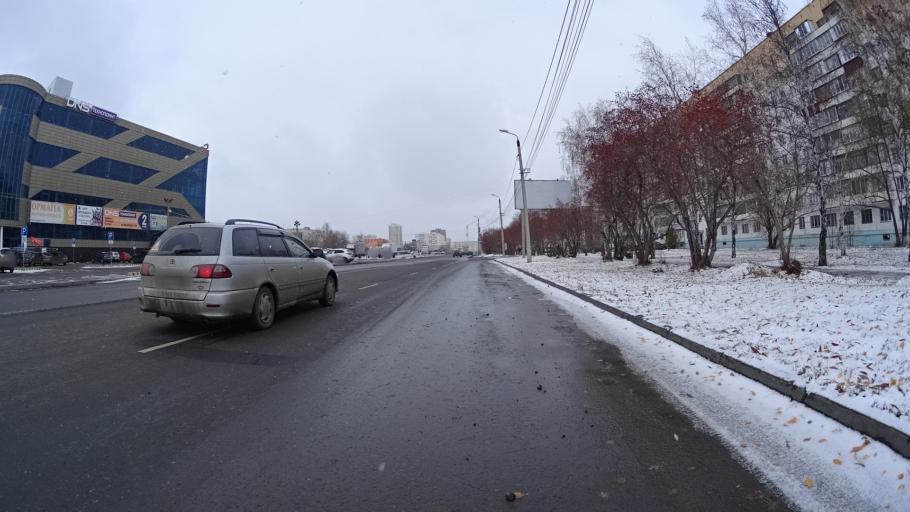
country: RU
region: Chelyabinsk
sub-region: Gorod Chelyabinsk
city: Chelyabinsk
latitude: 55.1899
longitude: 61.3215
